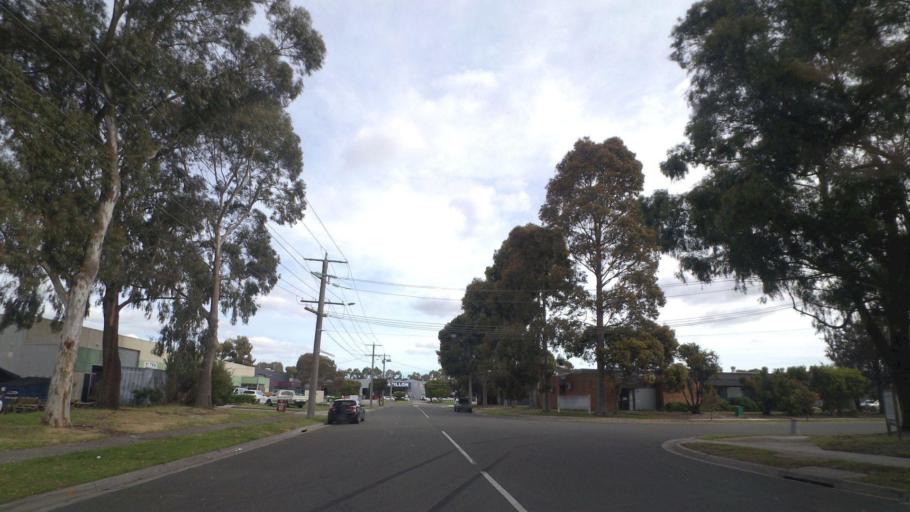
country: AU
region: Victoria
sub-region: Knox
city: Knoxfield
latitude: -37.8995
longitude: 145.2535
